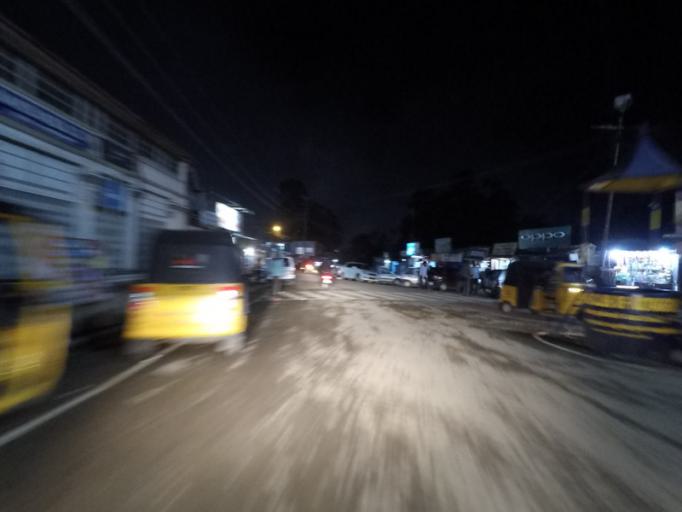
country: IN
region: Tamil Nadu
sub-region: Nilgiri
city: Kotagiri
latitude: 11.4257
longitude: 76.8659
